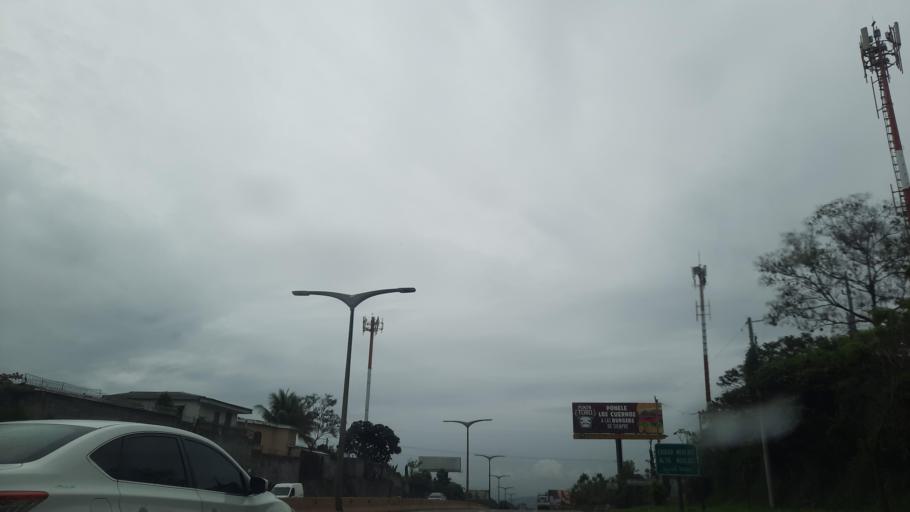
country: SV
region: La Libertad
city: Santa Tecla
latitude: 13.6845
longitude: -89.2736
